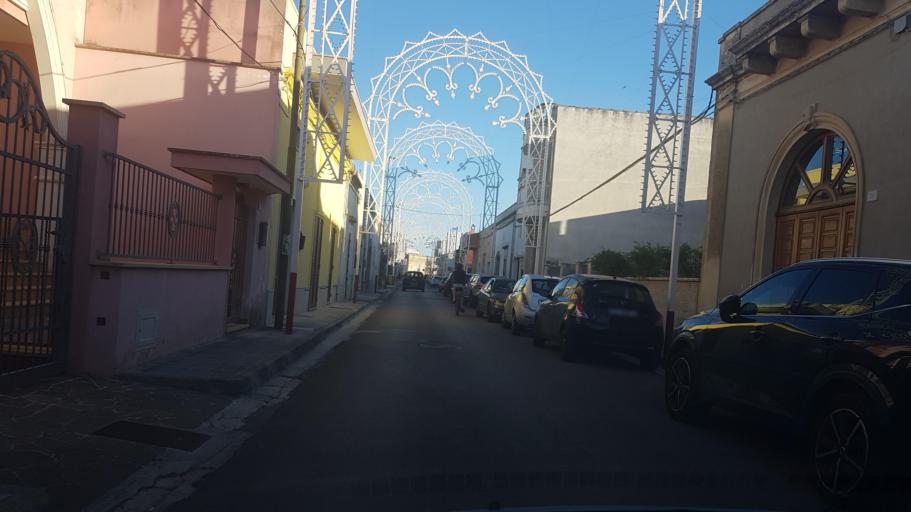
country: IT
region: Apulia
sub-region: Provincia di Lecce
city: Struda
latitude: 40.3202
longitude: 18.2821
